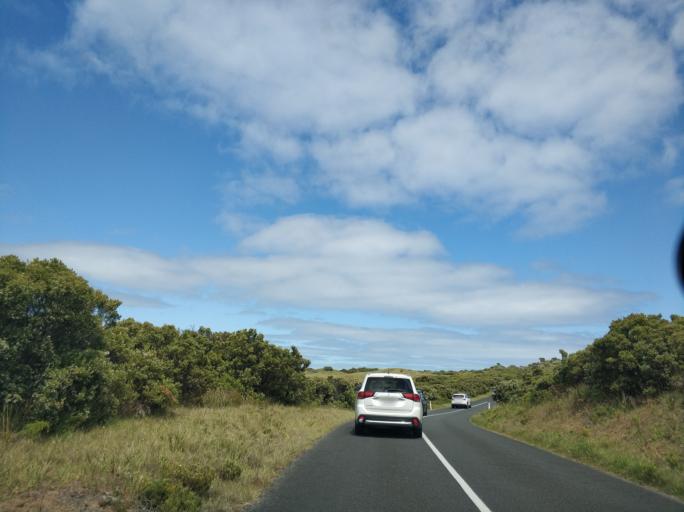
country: AU
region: Victoria
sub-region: Colac-Otway
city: Apollo Bay
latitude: -38.8511
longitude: 143.5299
